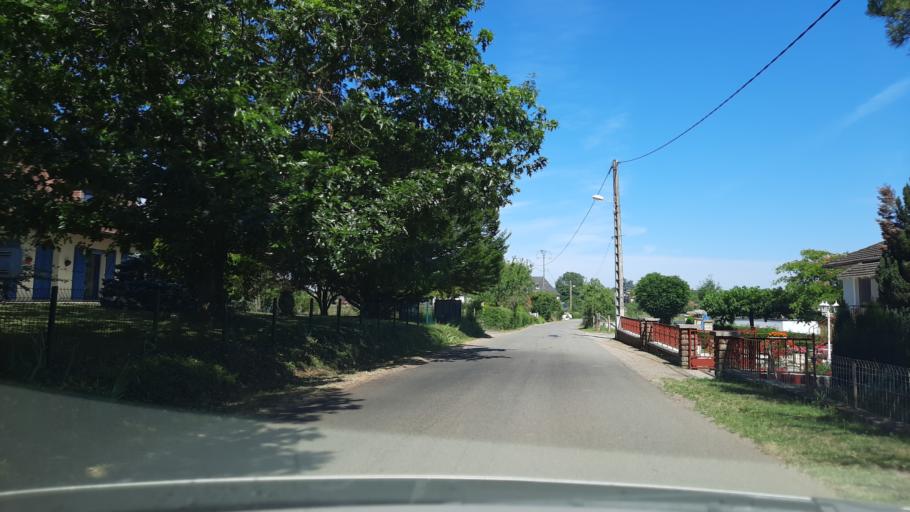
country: FR
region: Midi-Pyrenees
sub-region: Departement de l'Aveyron
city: Montbazens
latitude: 44.4948
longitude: 2.2268
